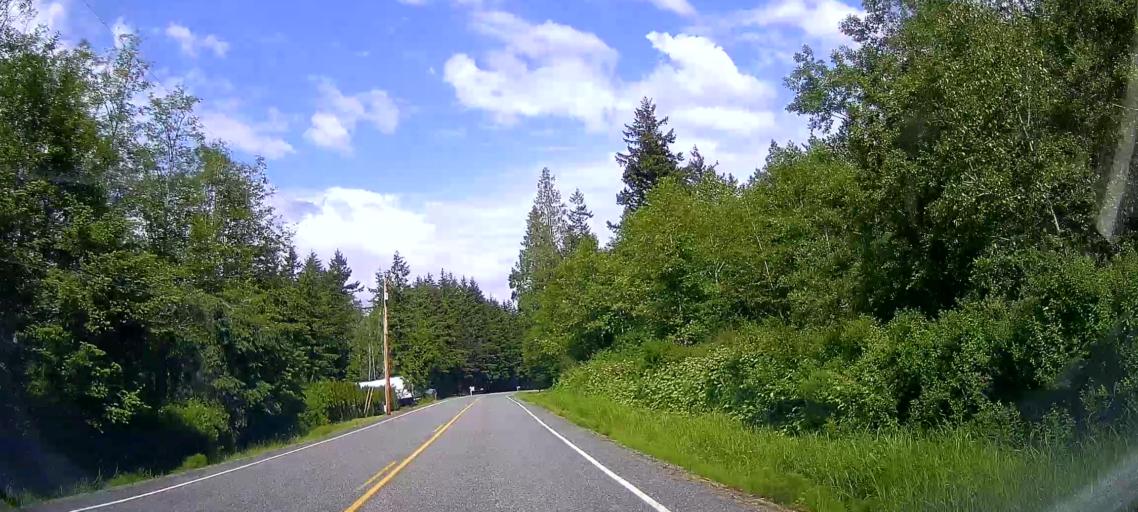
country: US
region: Washington
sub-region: Skagit County
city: Burlington
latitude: 48.5757
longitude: -122.3733
